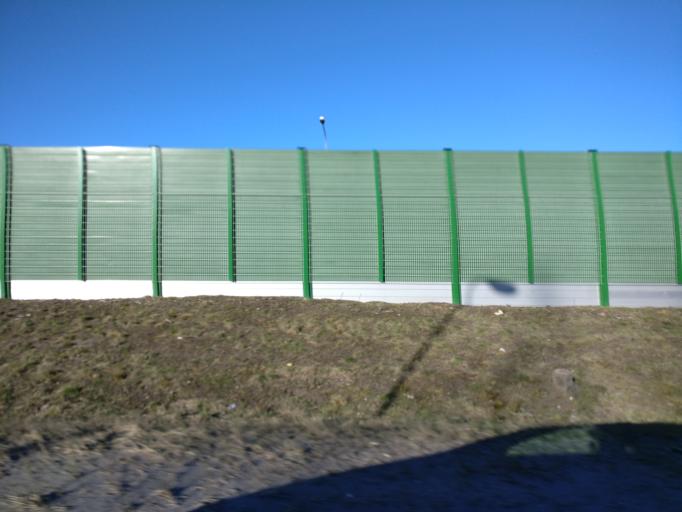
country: FI
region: Uusimaa
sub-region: Helsinki
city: Vantaa
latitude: 60.2362
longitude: 25.0465
